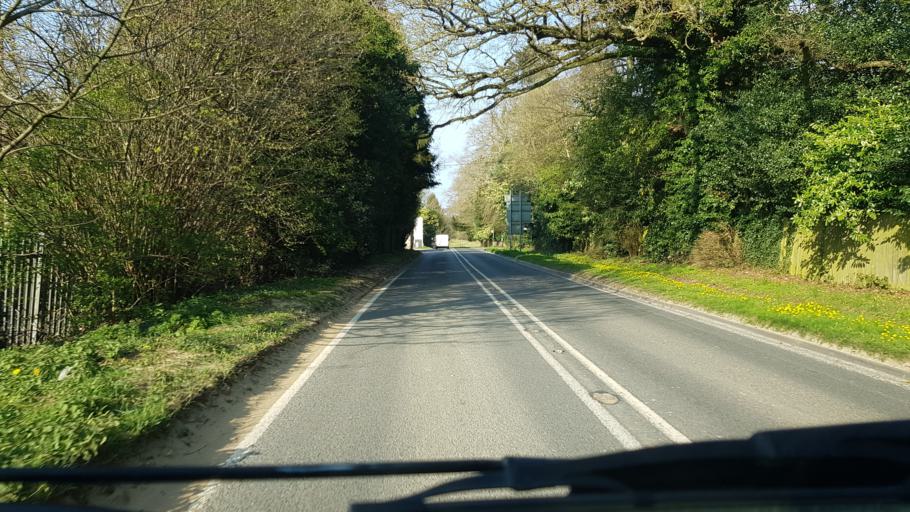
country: GB
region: England
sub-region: West Sussex
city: Petworth
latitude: 50.9601
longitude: -0.6255
